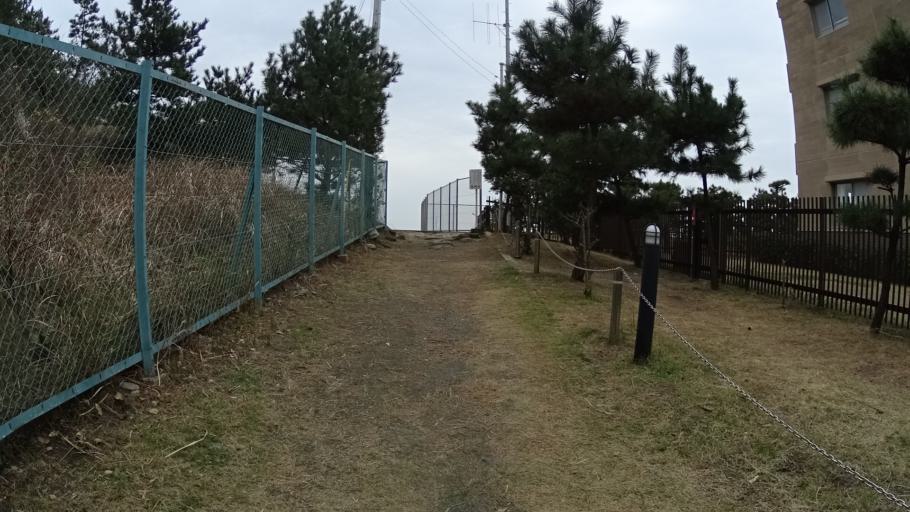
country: JP
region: Kanagawa
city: Oiso
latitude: 35.3060
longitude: 139.3055
